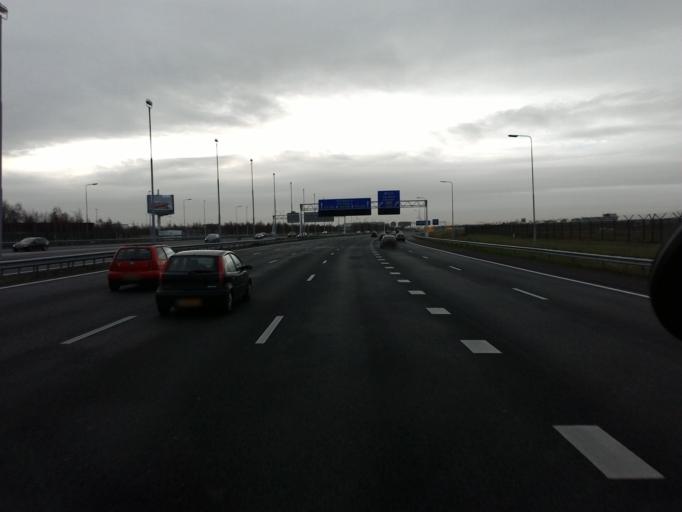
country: NL
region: North Holland
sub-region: Gemeente Aalsmeer
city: Aalsmeer
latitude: 52.3001
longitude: 4.7423
